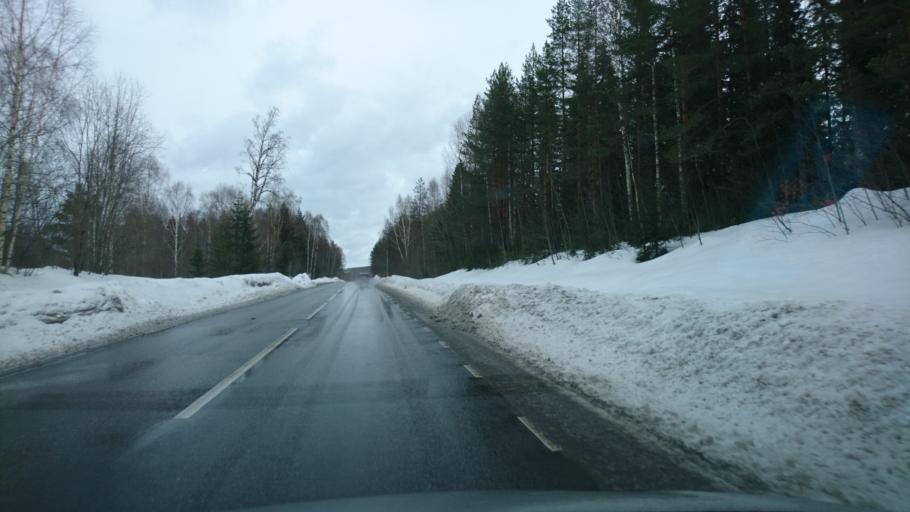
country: SE
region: Vaesternorrland
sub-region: Solleftea Kommun
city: Solleftea
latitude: 63.1494
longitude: 16.9703
